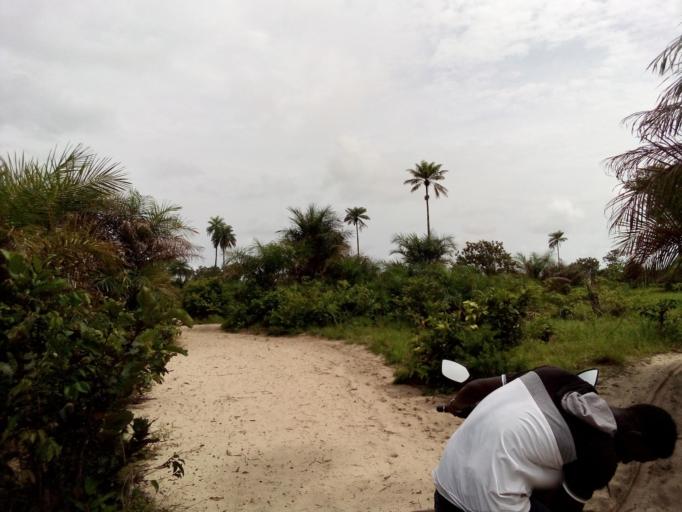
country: SL
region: Southern Province
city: Bonthe
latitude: 7.5177
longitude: -12.5708
